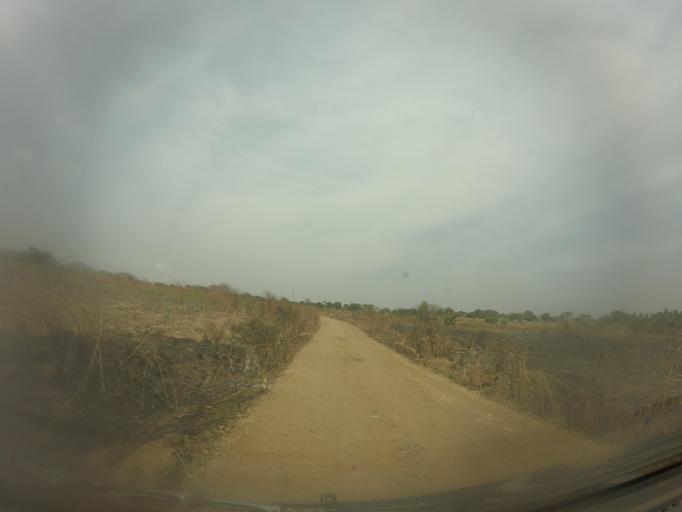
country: UG
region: Northern Region
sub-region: Arua District
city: Arua
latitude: 2.7678
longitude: 31.0352
